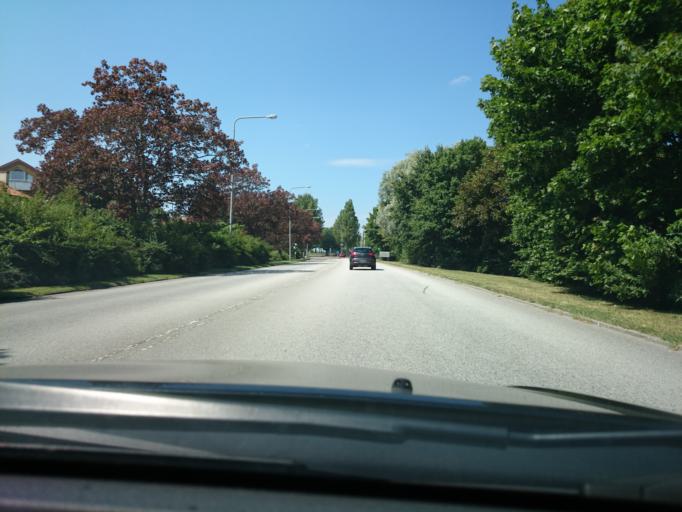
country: SE
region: Skane
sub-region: Landskrona
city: Landskrona
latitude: 55.8859
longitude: 12.8350
